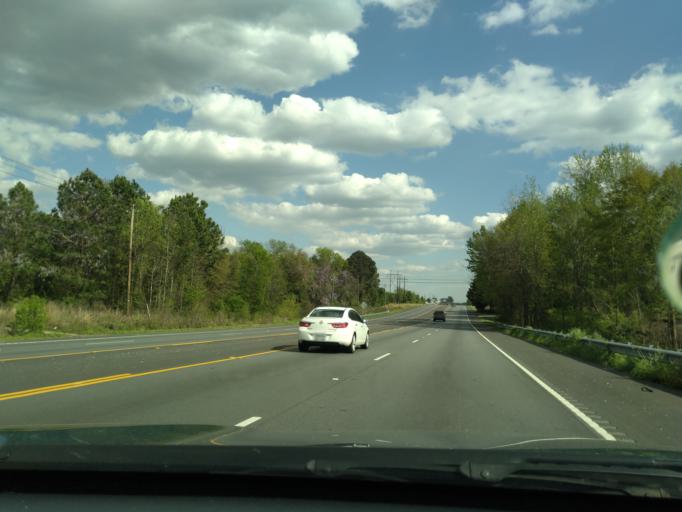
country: US
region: South Carolina
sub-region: Florence County
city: Florence
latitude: 34.2209
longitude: -79.7885
